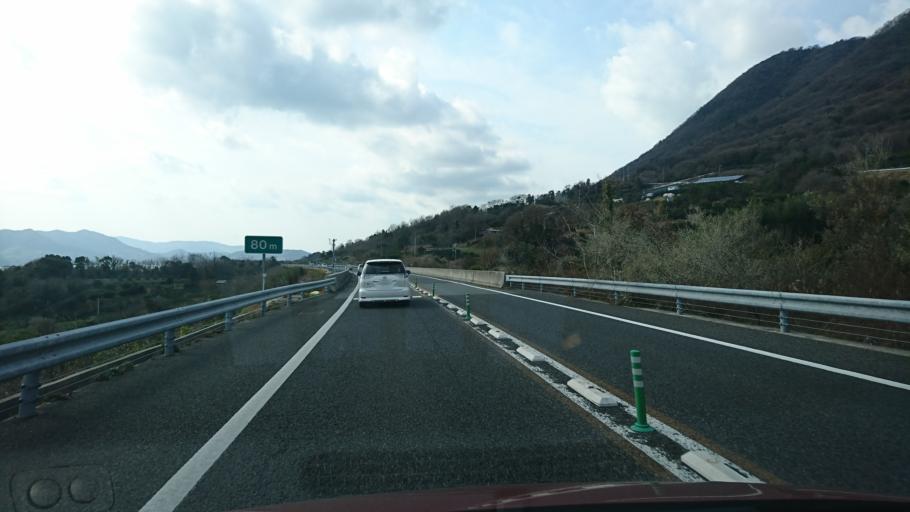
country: JP
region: Hiroshima
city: Innoshima
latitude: 34.2697
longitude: 133.0993
